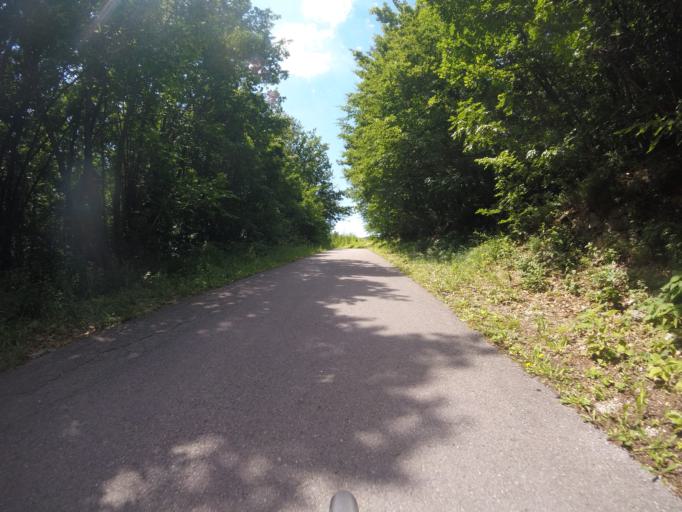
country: SI
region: Kostanjevica na Krki
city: Kostanjevica na Krki
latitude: 45.7648
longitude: 15.4052
